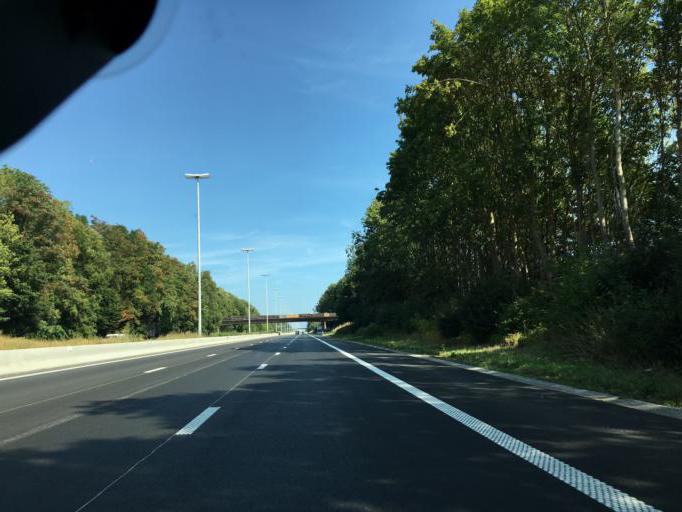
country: BE
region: Wallonia
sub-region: Province de Namur
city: Noville-les-Bois
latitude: 50.5320
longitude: 5.0271
